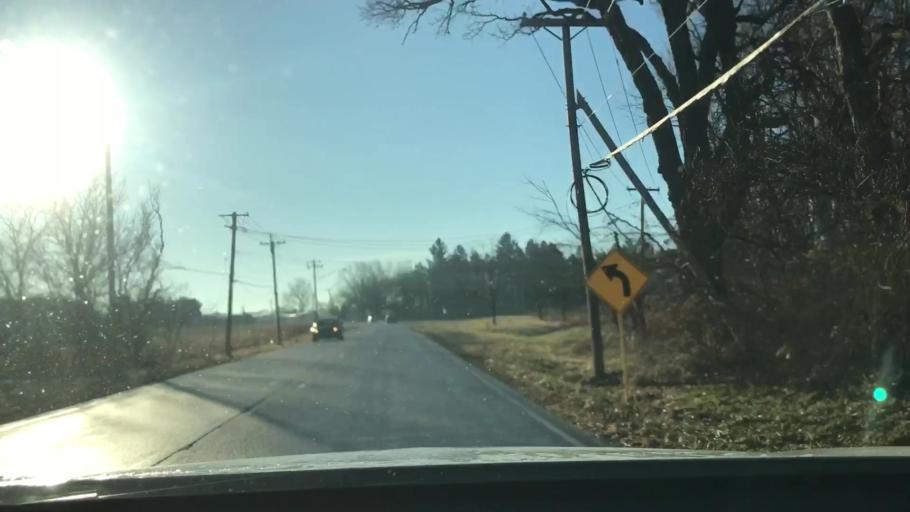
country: US
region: Illinois
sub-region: Kane County
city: Pingree Grove
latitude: 42.0928
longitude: -88.3994
